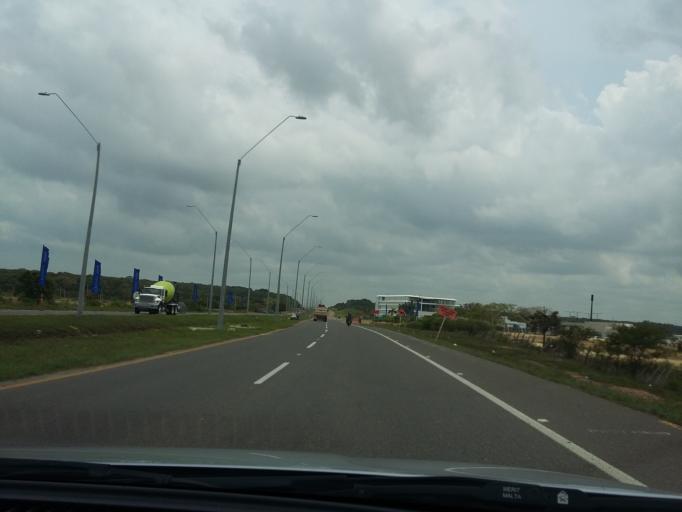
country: CO
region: Bolivar
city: Cartagena
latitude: 10.5034
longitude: -75.4742
